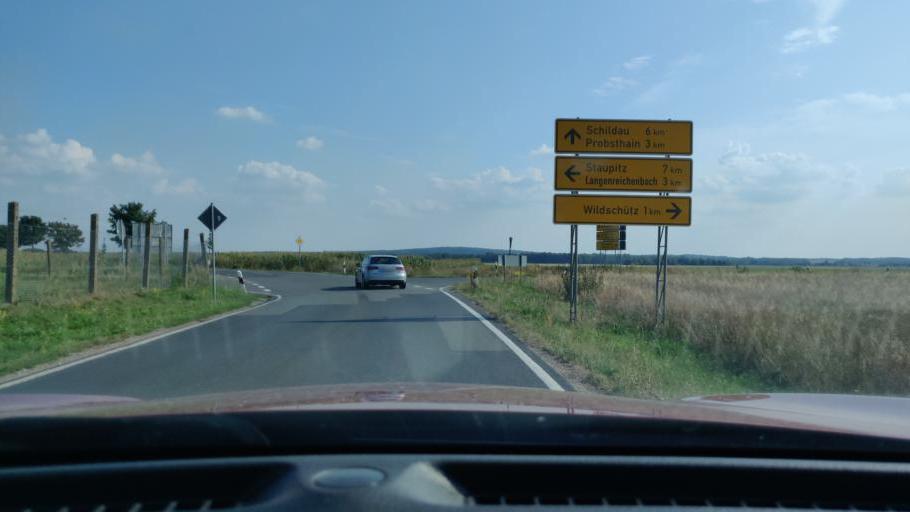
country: DE
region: Saxony
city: Mockrehna
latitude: 51.4842
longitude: 12.8692
